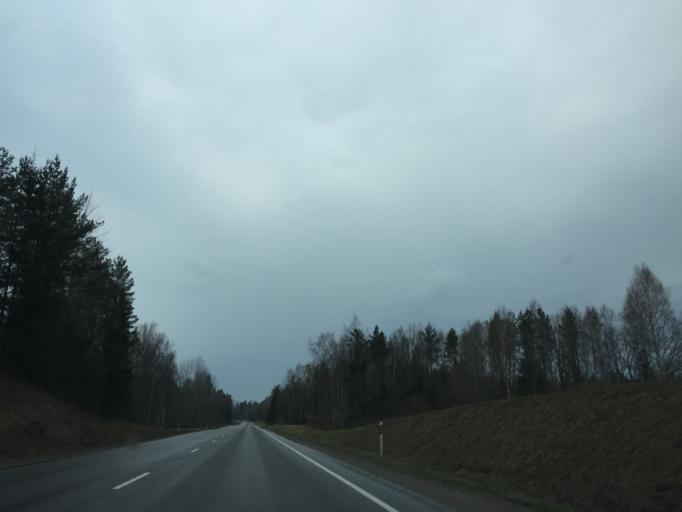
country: EE
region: Tartu
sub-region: UElenurme vald
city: Ulenurme
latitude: 58.1176
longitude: 26.7338
